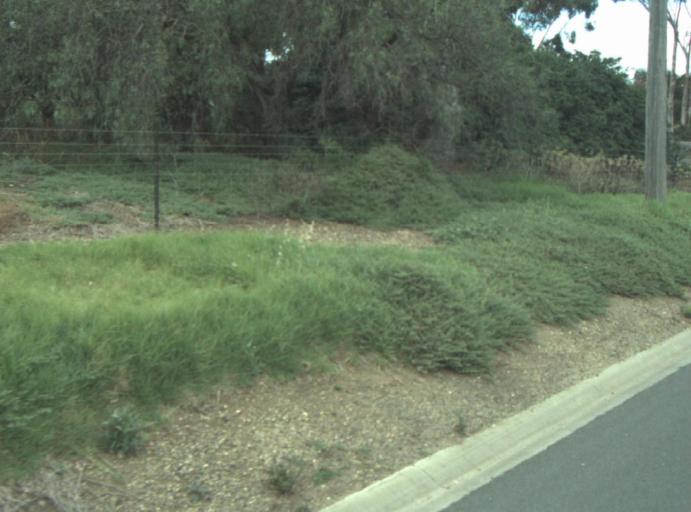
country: AU
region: Victoria
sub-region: Greater Geelong
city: Wandana Heights
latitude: -38.2066
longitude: 144.2876
